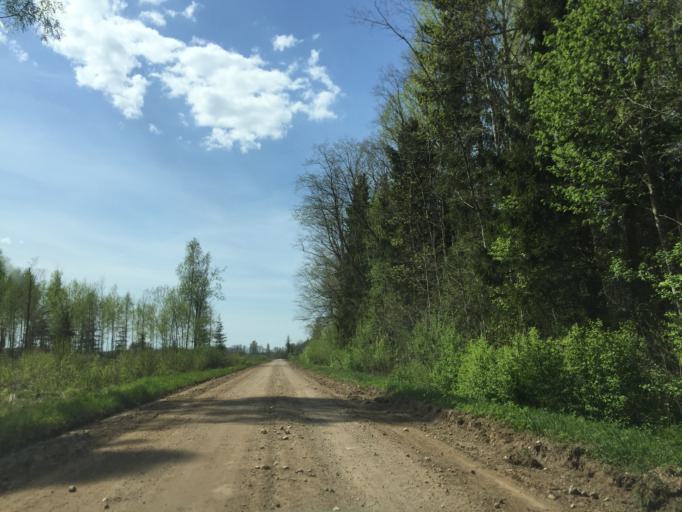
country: LV
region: Limbazu Rajons
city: Limbazi
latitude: 57.3875
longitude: 24.5935
